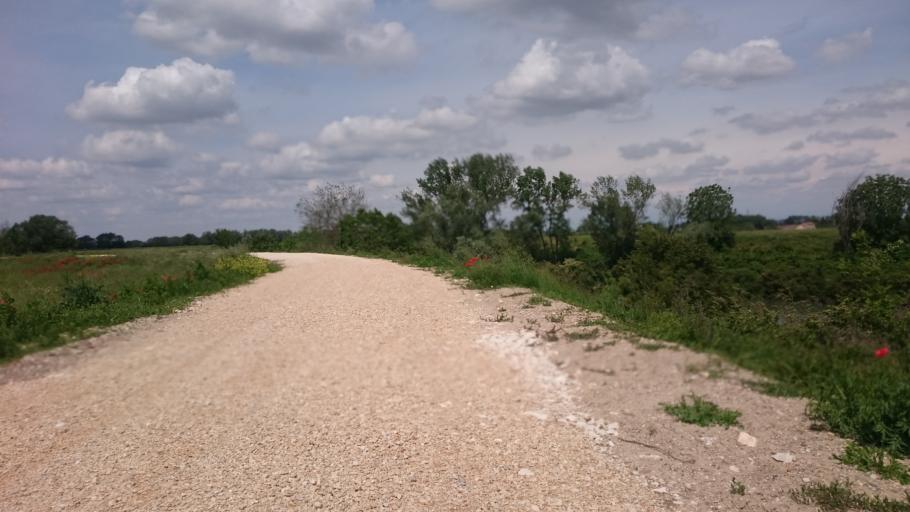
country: IT
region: Lombardy
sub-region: Provincia di Mantova
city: Roncoferraro
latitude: 45.0957
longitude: 10.9284
